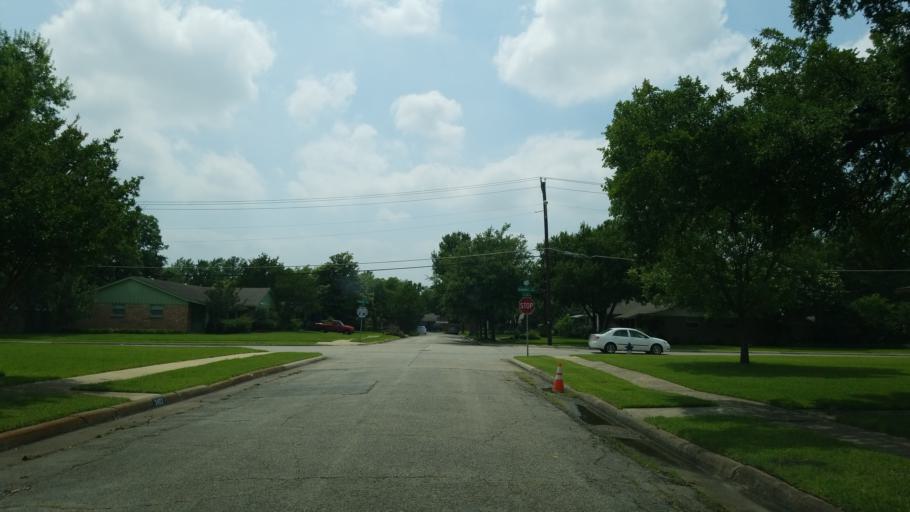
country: US
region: Texas
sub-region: Dallas County
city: Farmers Branch
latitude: 32.9069
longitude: -96.8636
